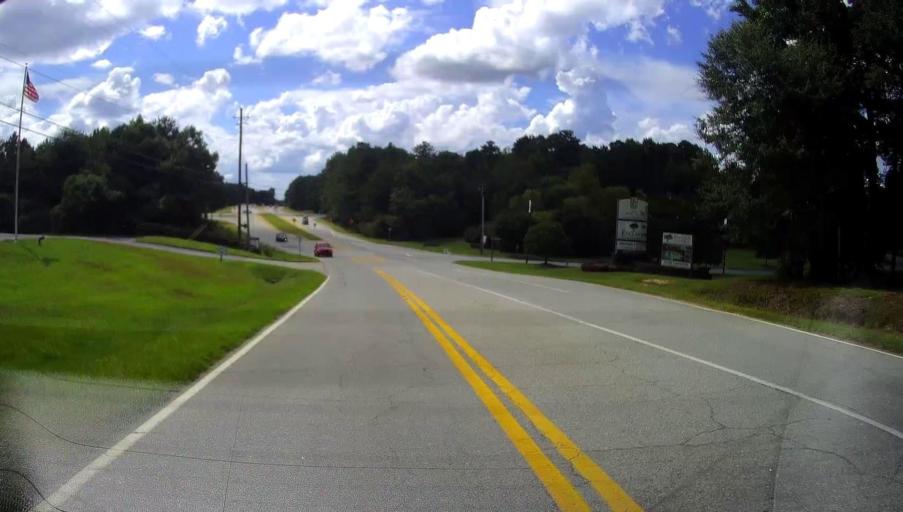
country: US
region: Alabama
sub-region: Russell County
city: Phenix City
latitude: 32.5660
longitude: -84.9580
